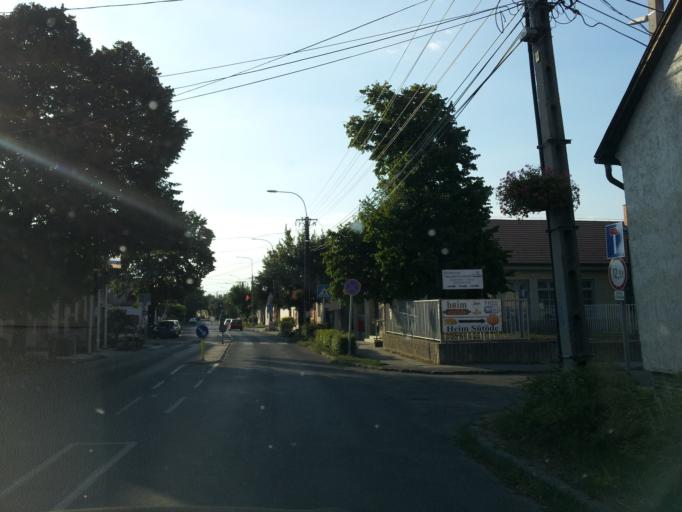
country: HU
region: Pest
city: Dunabogdany
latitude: 47.7941
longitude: 19.0358
